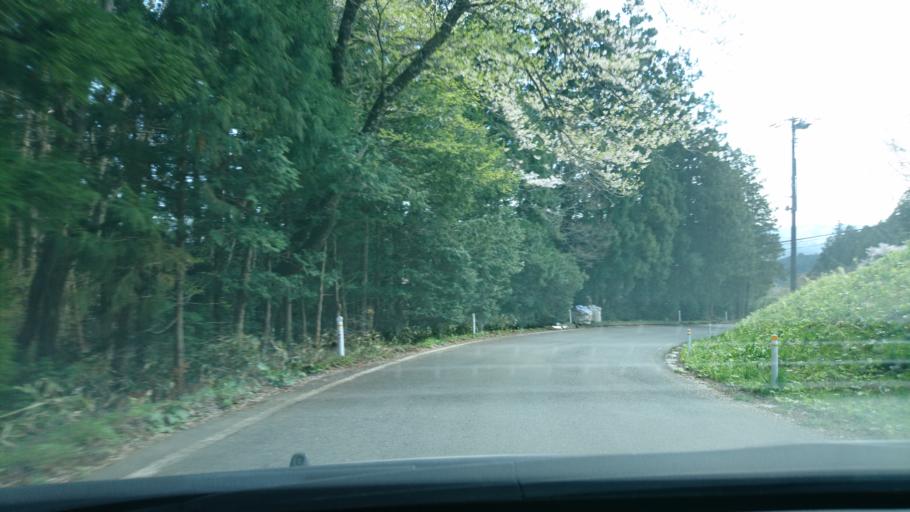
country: JP
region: Iwate
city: Ofunato
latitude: 38.9547
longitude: 141.4522
